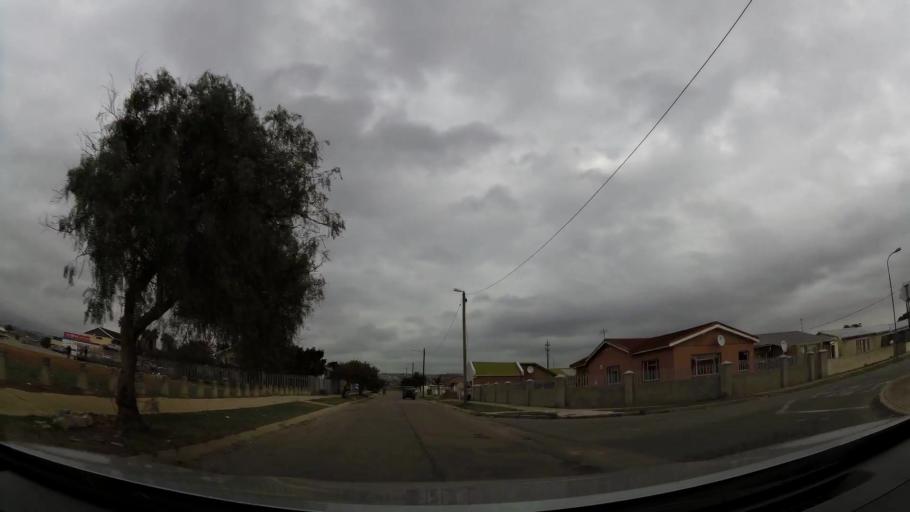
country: ZA
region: Eastern Cape
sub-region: Nelson Mandela Bay Metropolitan Municipality
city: Port Elizabeth
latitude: -33.9008
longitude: 25.5629
